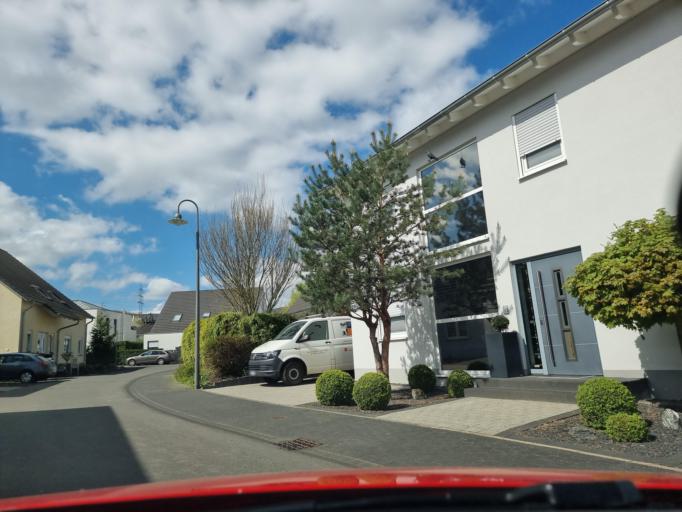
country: DE
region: Rheinland-Pfalz
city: Longuich
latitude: 49.7916
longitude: 6.7956
